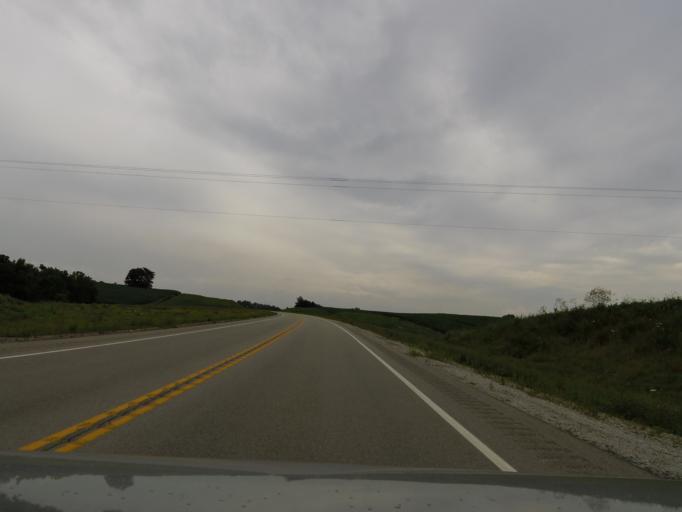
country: US
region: Ohio
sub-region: Brown County
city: Aberdeen
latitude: 38.6195
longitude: -83.8389
